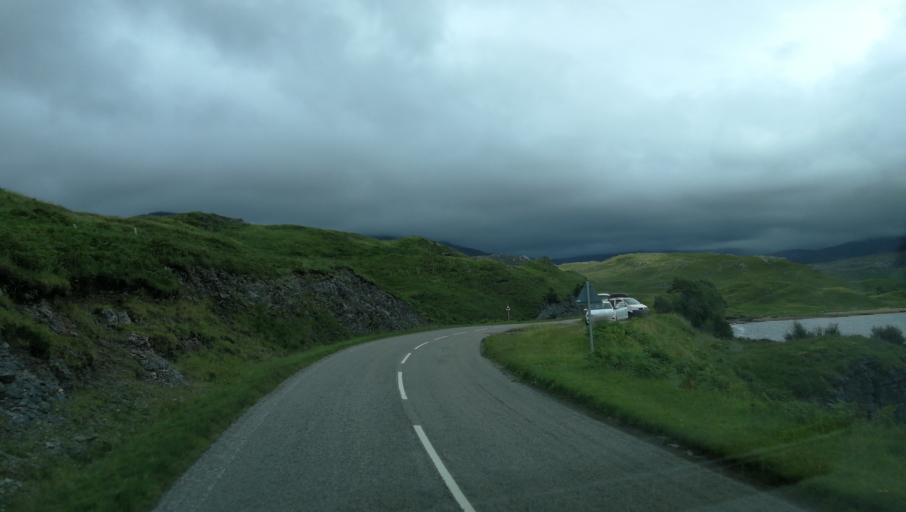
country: GB
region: Scotland
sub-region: Highland
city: Ullapool
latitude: 58.1696
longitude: -4.9953
